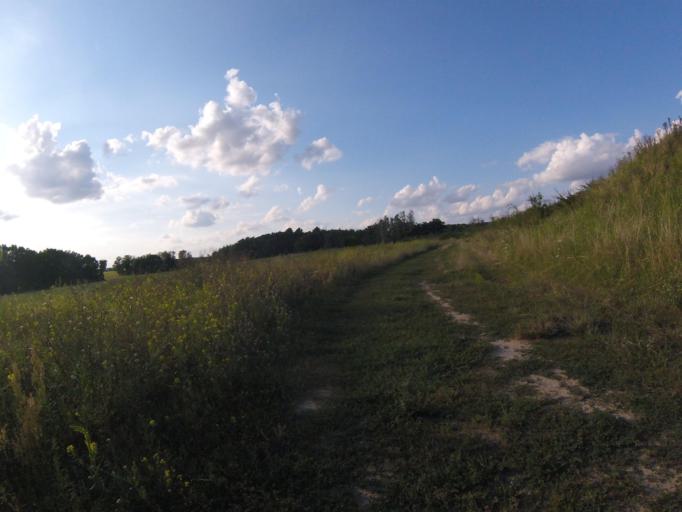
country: DE
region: Brandenburg
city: Mittenwalde
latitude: 52.2759
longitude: 13.5131
